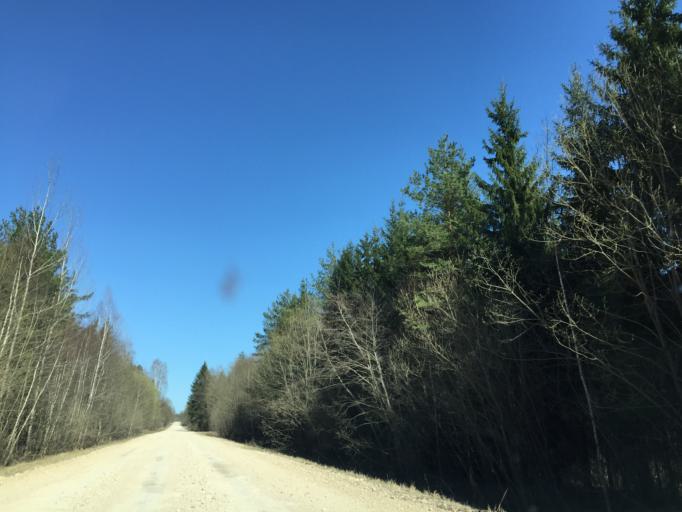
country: LV
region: Malpils
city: Malpils
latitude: 57.0320
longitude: 25.0457
